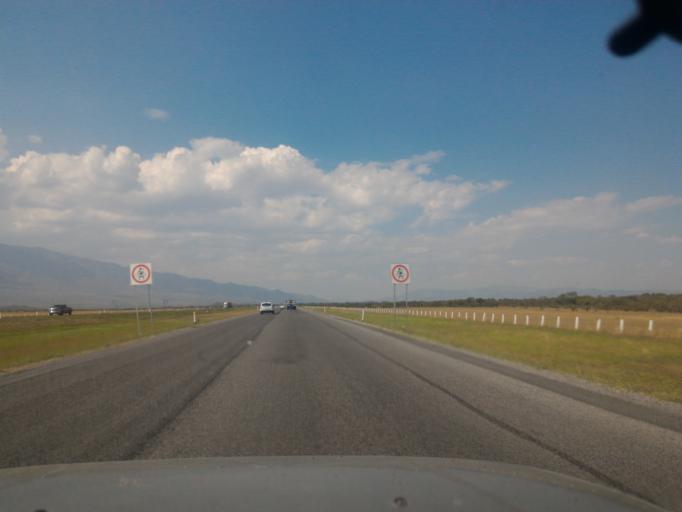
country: MX
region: Jalisco
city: Atoyac
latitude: 19.9672
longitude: -103.5341
